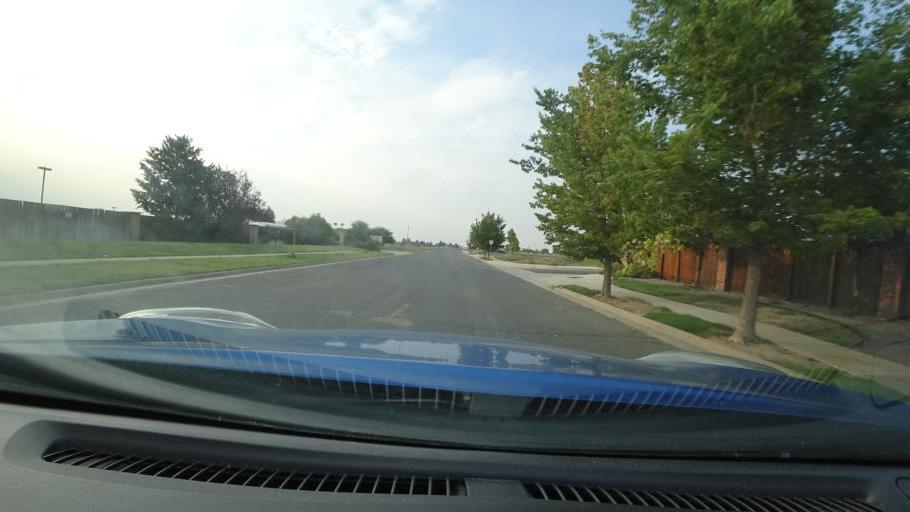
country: US
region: Colorado
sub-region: Adams County
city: Aurora
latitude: 39.7268
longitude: -104.7861
